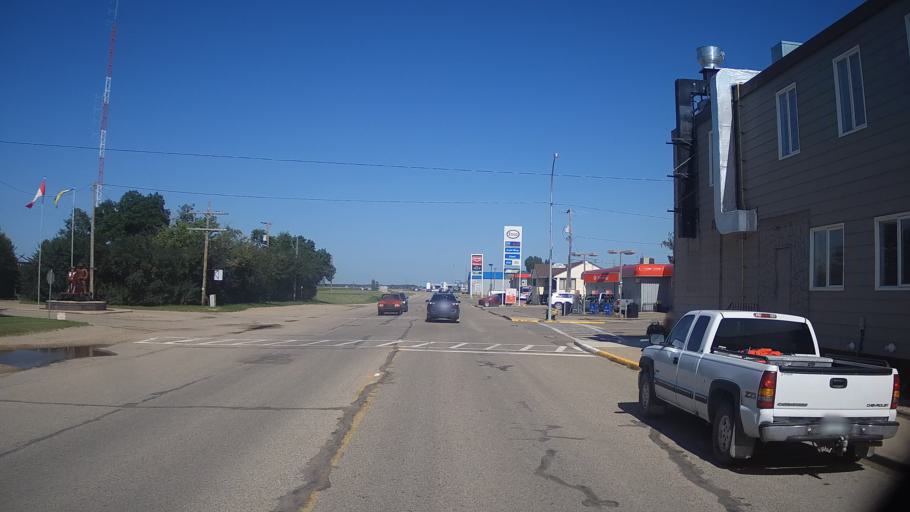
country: CA
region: Saskatchewan
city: Watrous
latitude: 51.6719
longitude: -105.4685
